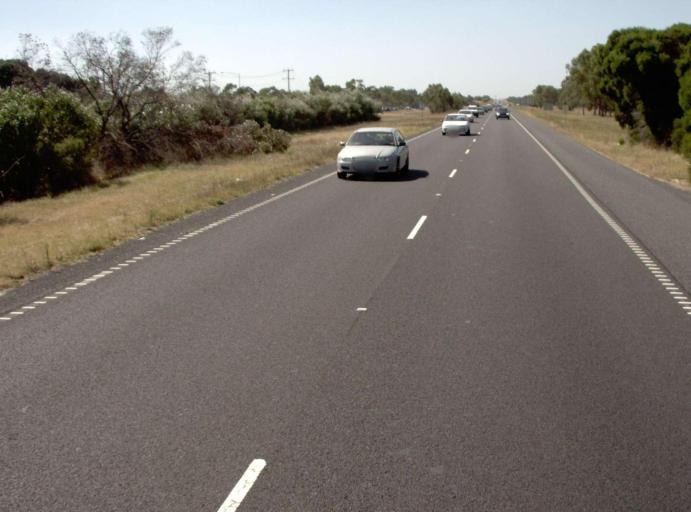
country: AU
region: Victoria
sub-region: Kingston
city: Patterson Lakes
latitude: -38.0535
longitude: 145.1456
